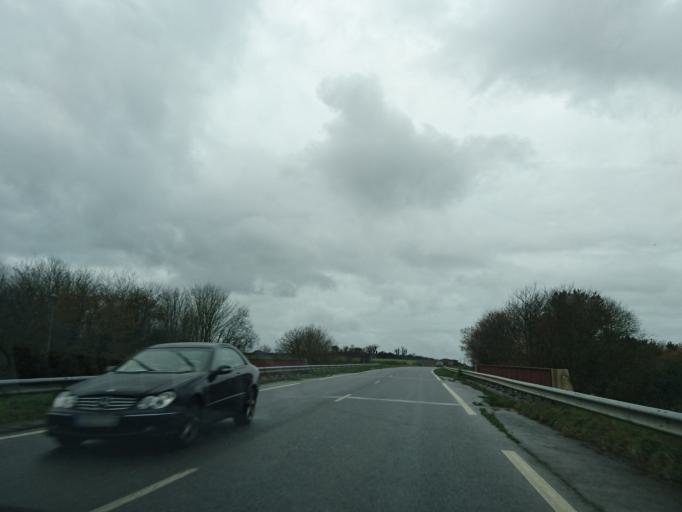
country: FR
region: Brittany
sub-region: Departement du Finistere
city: Plouzane
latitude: 48.3594
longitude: -4.6423
